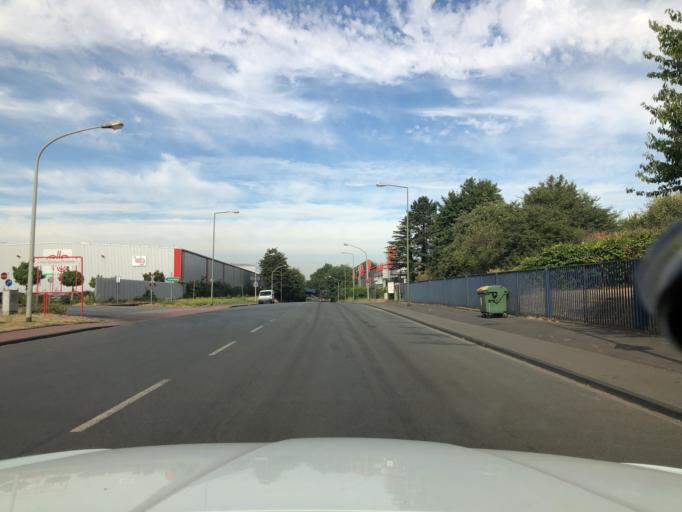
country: DE
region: North Rhine-Westphalia
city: Meiderich
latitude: 51.4580
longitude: 6.7853
